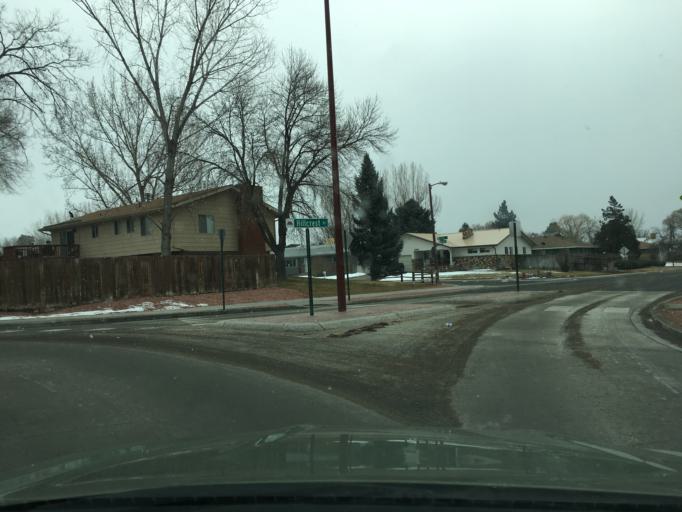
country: US
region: Colorado
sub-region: Montrose County
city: Montrose
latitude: 38.4745
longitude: -107.8567
